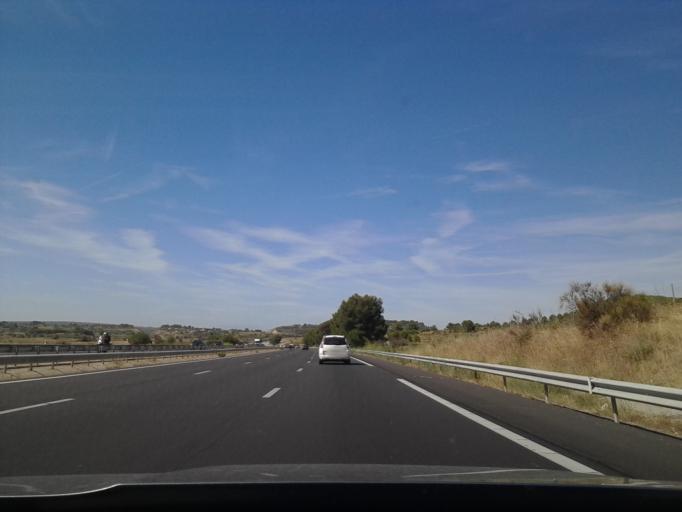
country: FR
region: Languedoc-Roussillon
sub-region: Departement de l'Herault
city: Lespignan
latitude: 43.2932
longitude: 3.1957
